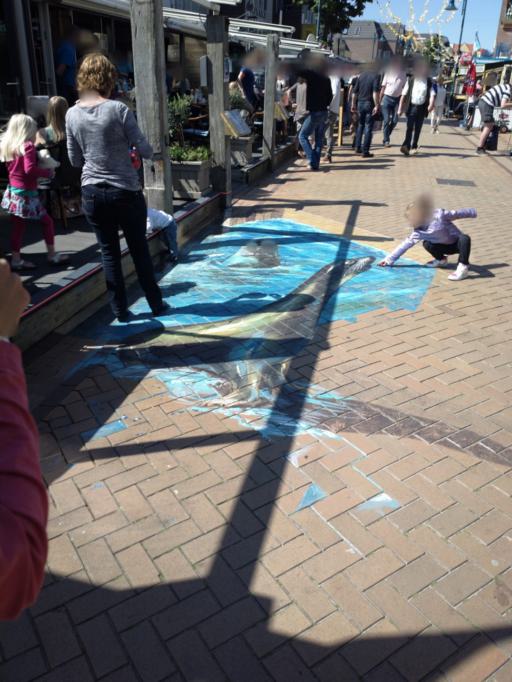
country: NL
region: North Holland
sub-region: Gemeente Texel
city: Den Burg
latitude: 53.0984
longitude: 4.7625
